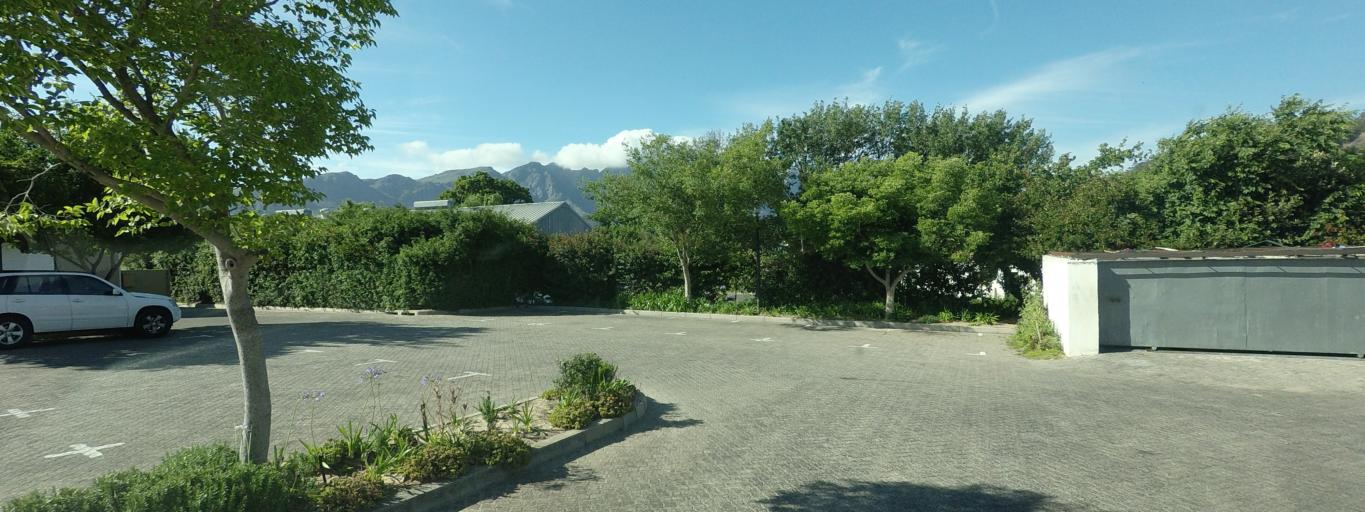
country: ZA
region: Western Cape
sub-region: Cape Winelands District Municipality
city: Paarl
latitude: -33.9067
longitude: 19.1145
